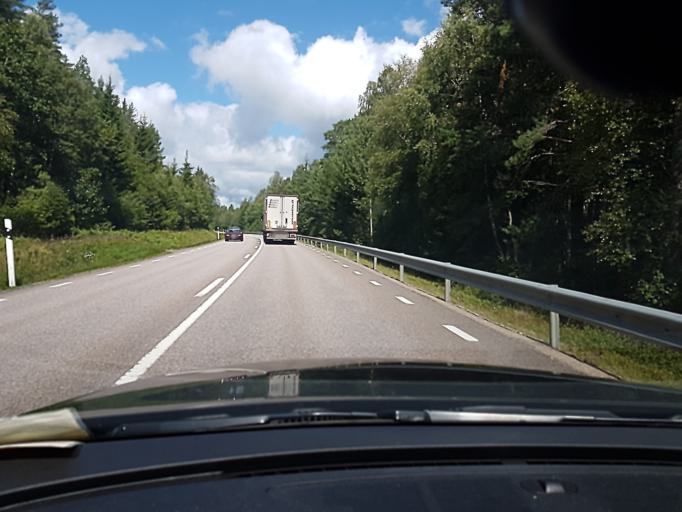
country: SE
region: Kronoberg
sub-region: Lessebo Kommun
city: Lessebo
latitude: 56.7751
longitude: 15.2550
